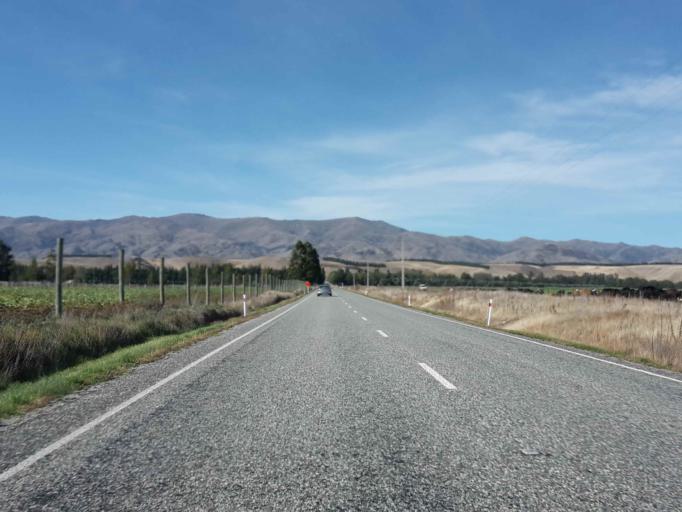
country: NZ
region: Otago
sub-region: Queenstown-Lakes District
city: Wanaka
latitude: -44.8279
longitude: 169.3673
